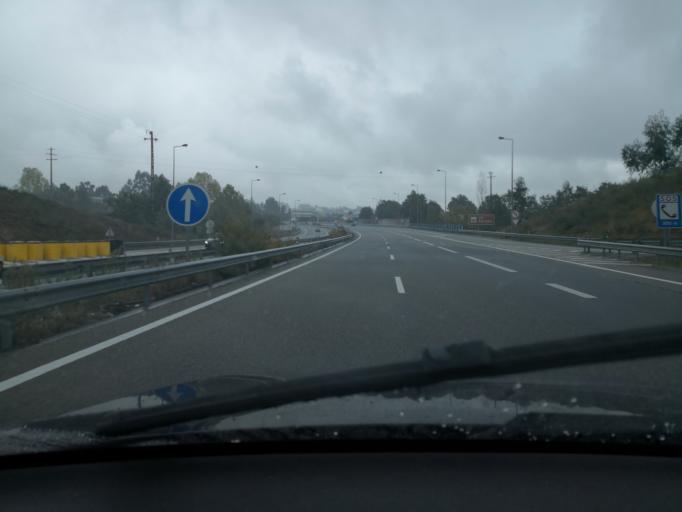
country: PT
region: Porto
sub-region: Pacos de Ferreira
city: Frazao
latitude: 41.2572
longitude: -8.3972
